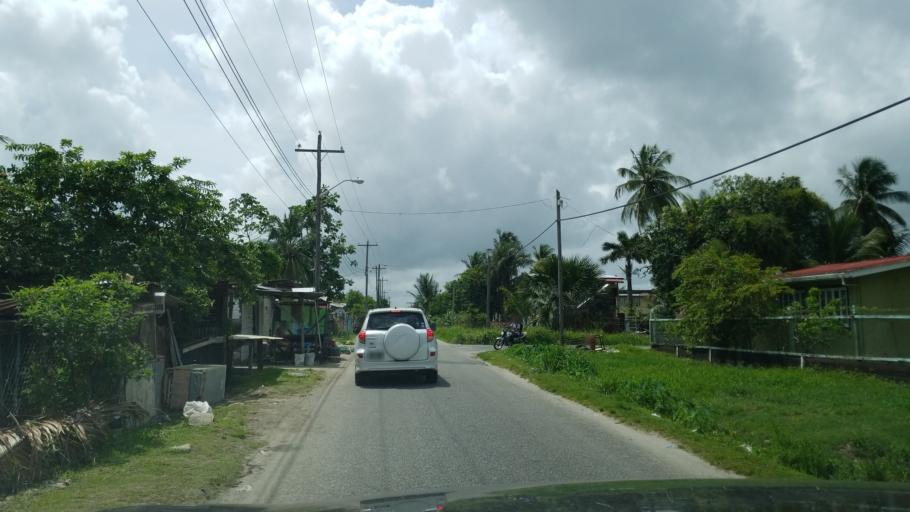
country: GY
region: Demerara-Mahaica
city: Georgetown
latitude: 6.7924
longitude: -58.1502
